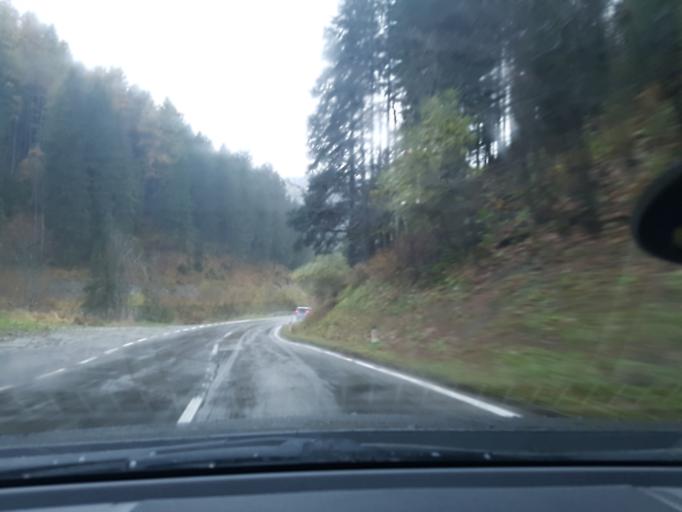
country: AT
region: Styria
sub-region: Politischer Bezirk Murtal
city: Hohentauern
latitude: 47.4563
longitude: 14.4908
